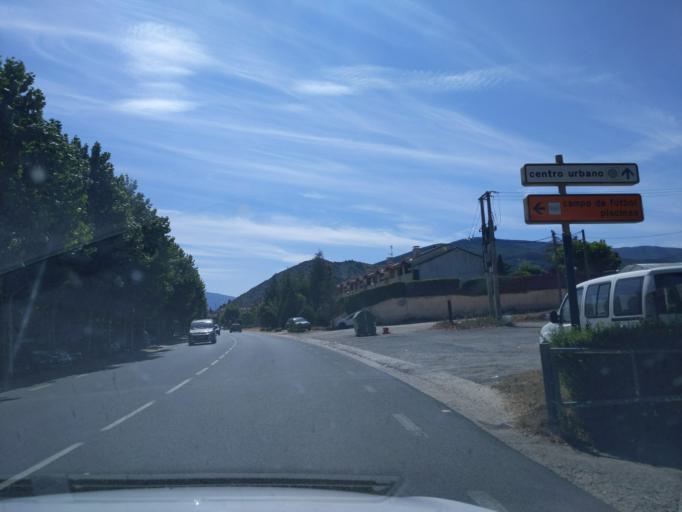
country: ES
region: La Rioja
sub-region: Provincia de La Rioja
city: Ezcaray
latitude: 42.3327
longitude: -3.0127
